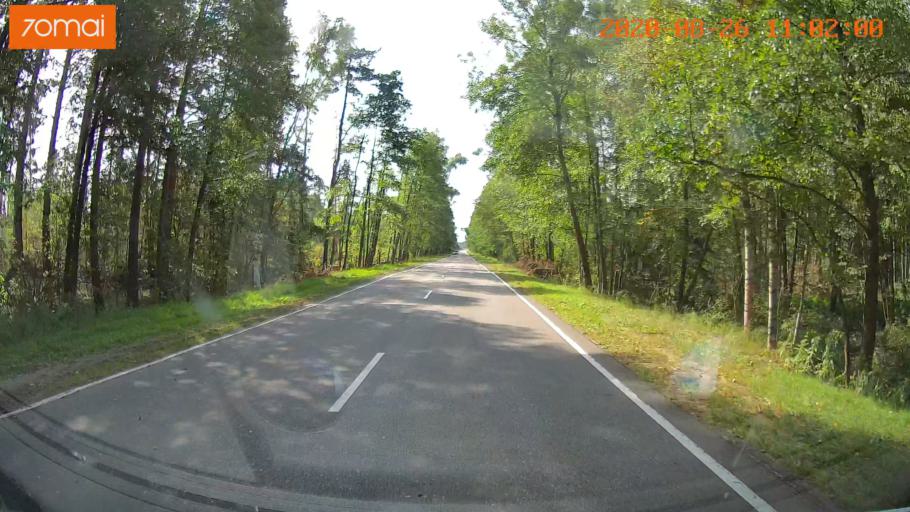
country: RU
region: Rjazan
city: Izhevskoye
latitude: 54.5564
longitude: 41.2265
